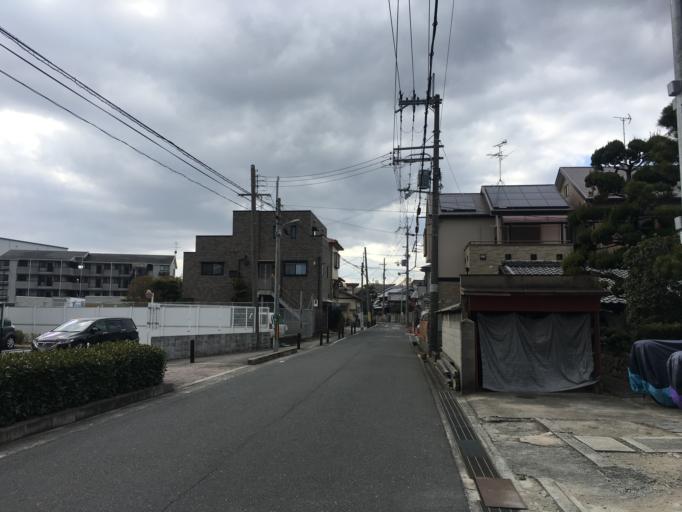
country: JP
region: Osaka
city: Ibaraki
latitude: 34.8396
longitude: 135.5542
